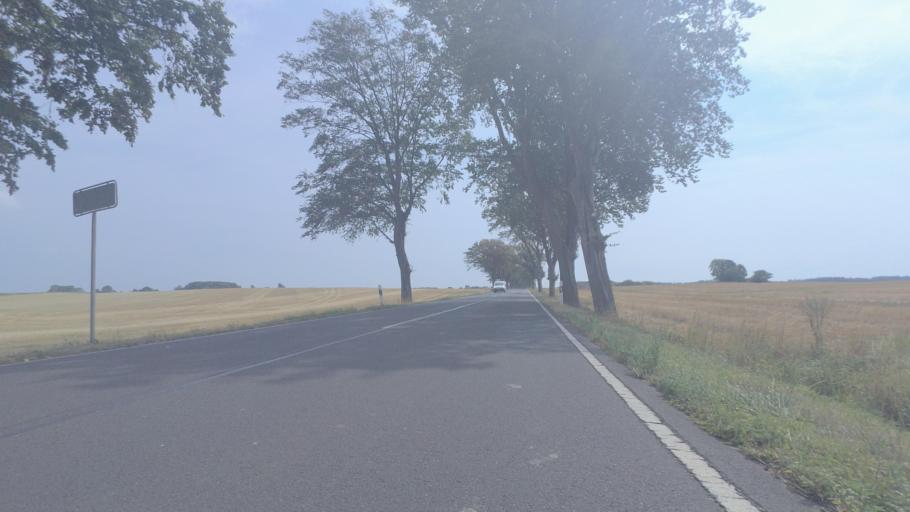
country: DE
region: Mecklenburg-Vorpommern
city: Samtens
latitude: 54.3450
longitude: 13.3064
